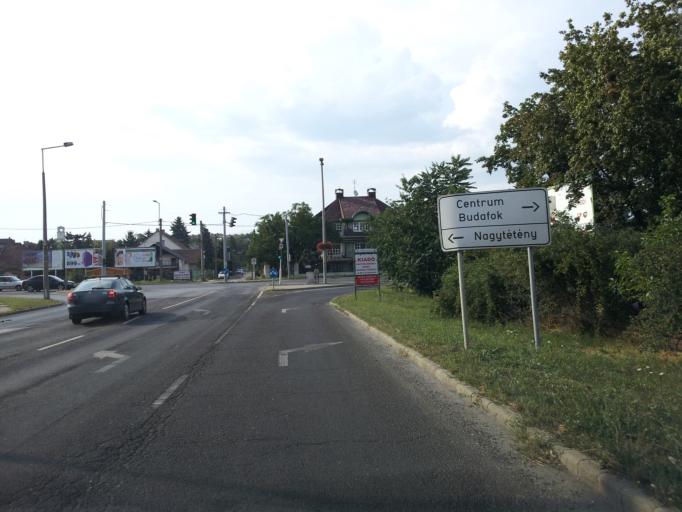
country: HU
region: Budapest
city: Budapest XXII. keruelet
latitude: 47.4103
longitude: 19.0230
